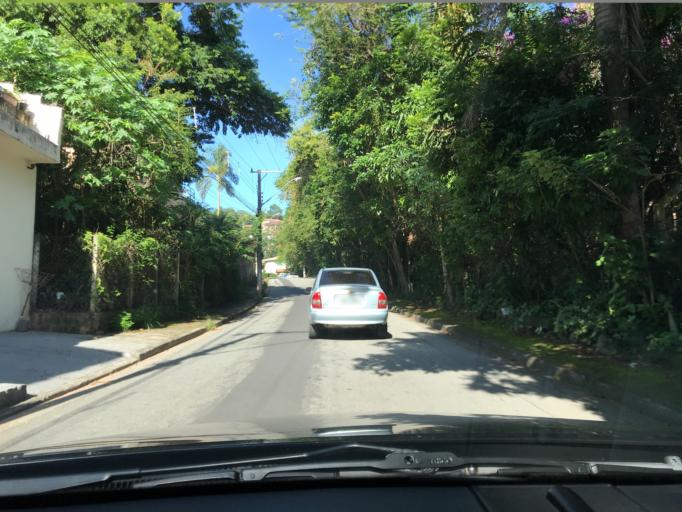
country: BR
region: Sao Paulo
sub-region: Itapevi
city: Itapevi
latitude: -23.5355
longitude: -46.9421
